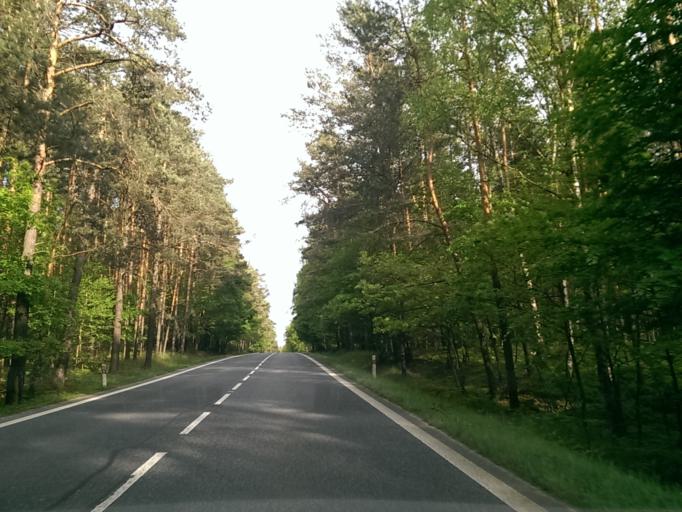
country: CZ
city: Doksy
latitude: 50.5289
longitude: 14.6946
